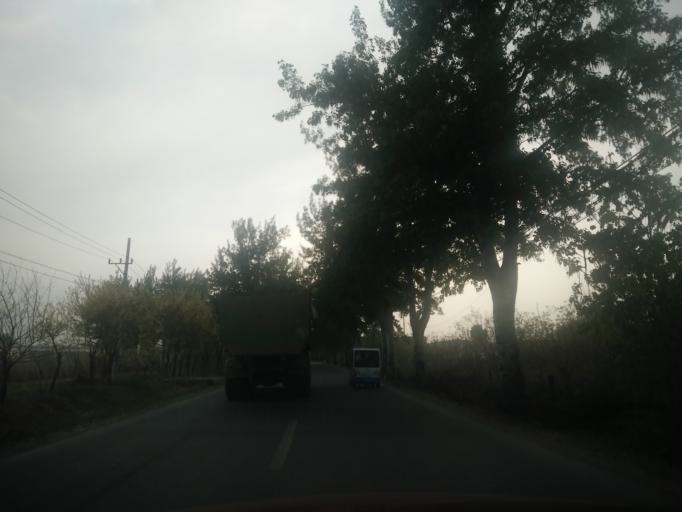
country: CN
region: Beijing
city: Qingyundian
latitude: 39.6791
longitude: 116.4612
